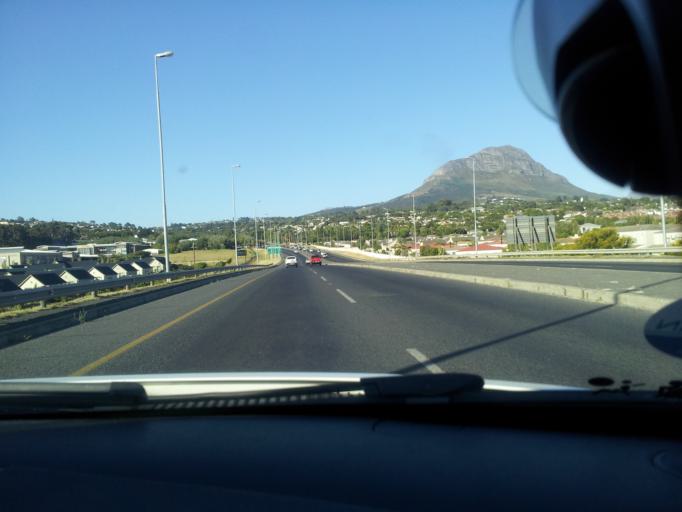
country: ZA
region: Western Cape
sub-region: Cape Winelands District Municipality
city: Stellenbosch
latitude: -34.0740
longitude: 18.8228
